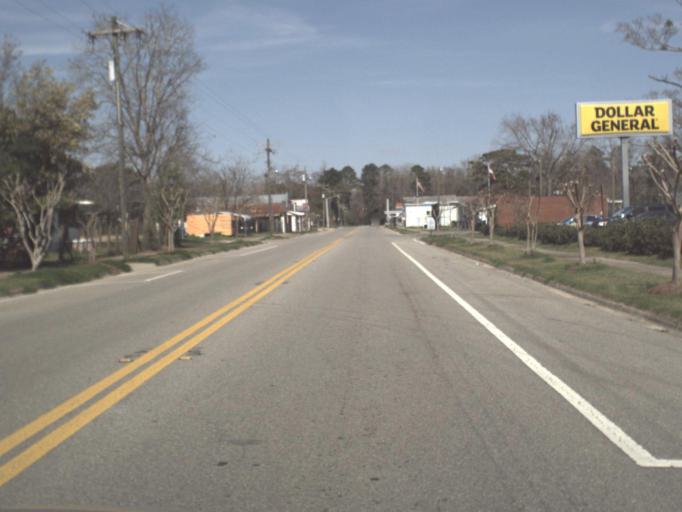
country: US
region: Florida
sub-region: Gadsden County
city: Gretna
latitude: 30.5677
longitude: -84.7436
